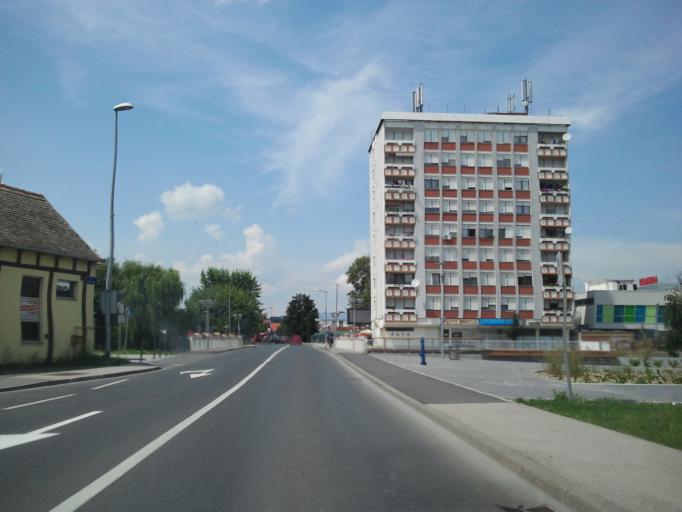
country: HR
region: Vukovarsko-Srijemska
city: Vukovar
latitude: 45.3507
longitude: 19.0016
